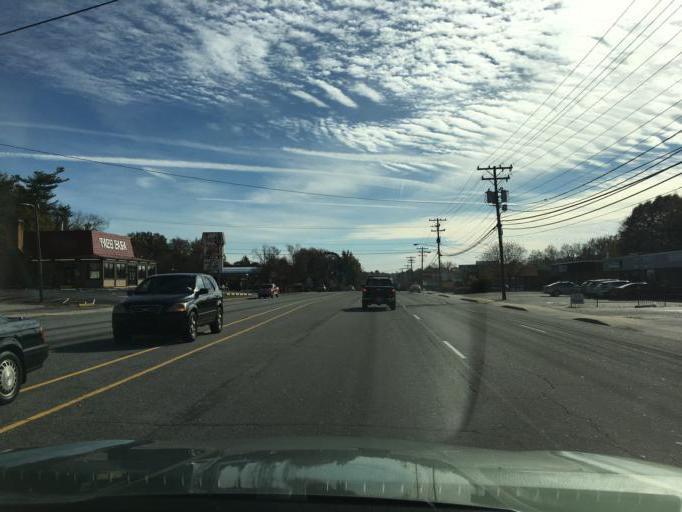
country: US
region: South Carolina
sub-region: Greenville County
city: Greenville
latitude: 34.8678
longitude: -82.3581
